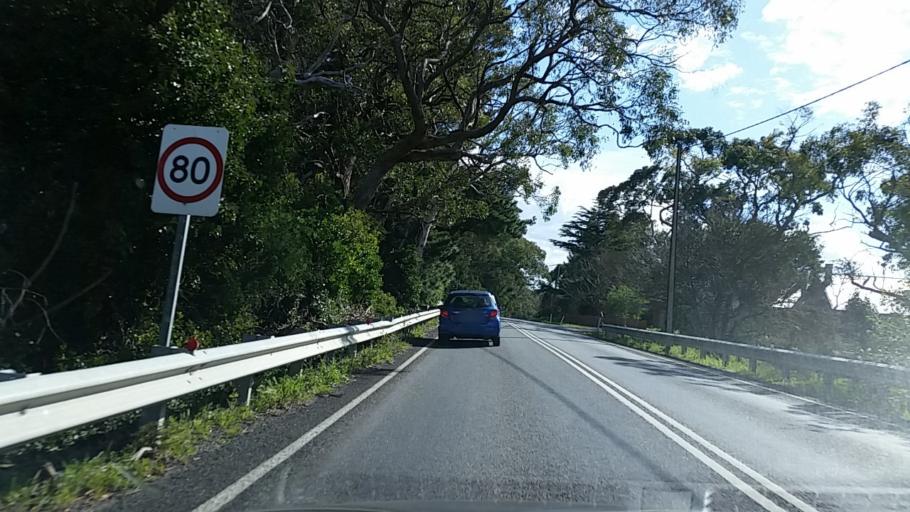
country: AU
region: South Australia
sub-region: Alexandrina
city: Mount Compass
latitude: -35.2908
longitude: 138.5831
